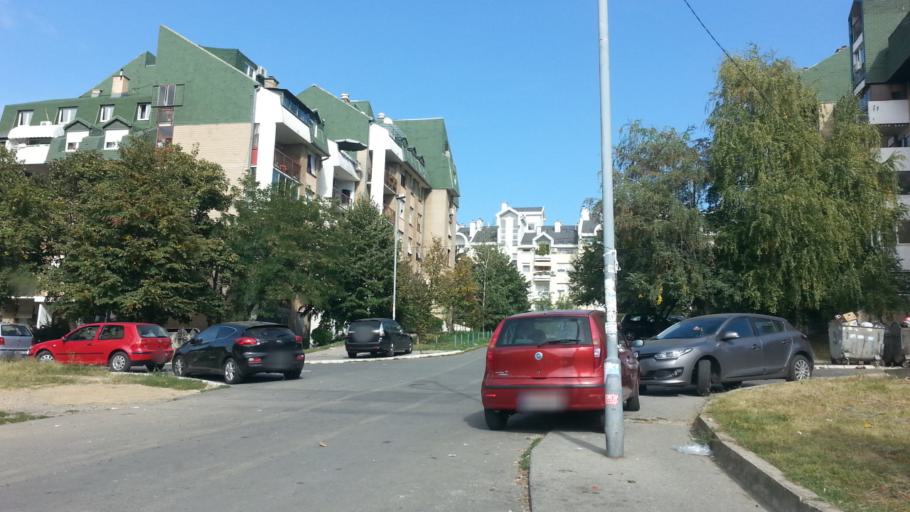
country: RS
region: Central Serbia
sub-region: Belgrade
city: Rakovica
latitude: 44.7489
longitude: 20.4292
